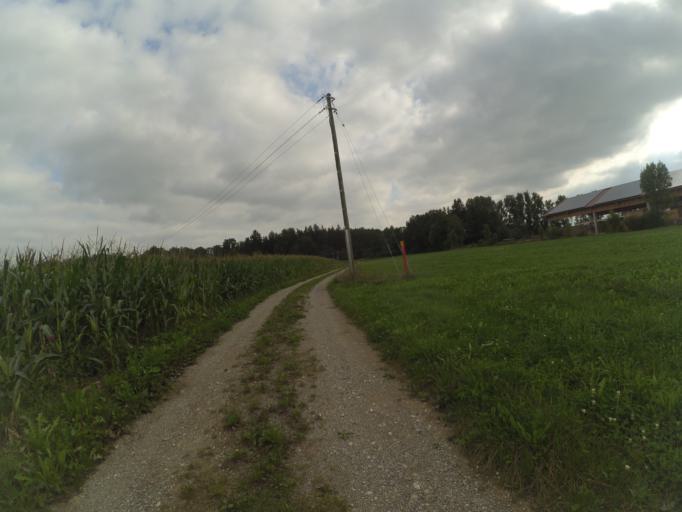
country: DE
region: Bavaria
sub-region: Upper Bavaria
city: Hurlach
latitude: 48.0691
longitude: 10.7950
